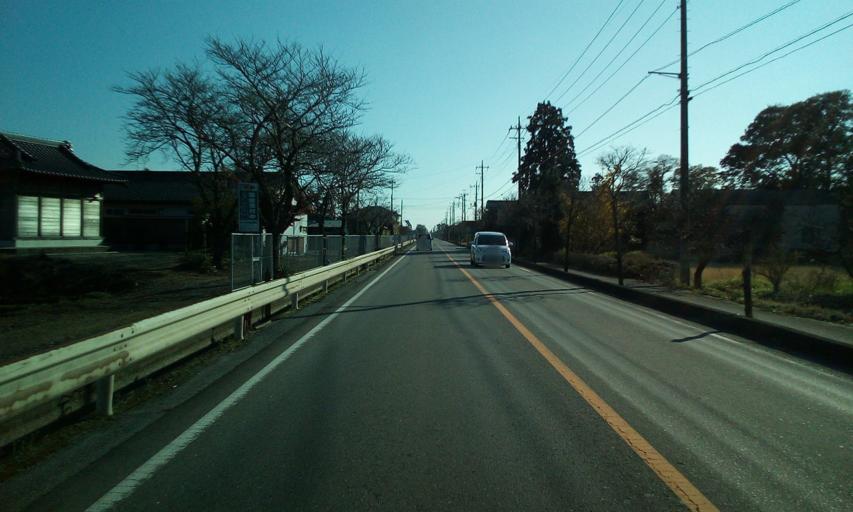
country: JP
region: Saitama
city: Sugito
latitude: 36.0296
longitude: 139.7879
